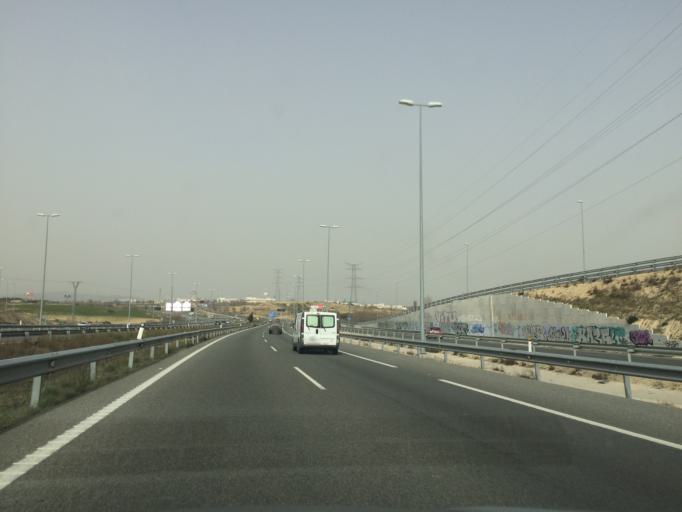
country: ES
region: Madrid
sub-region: Provincia de Madrid
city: Las Rozas de Madrid
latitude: 40.4882
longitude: -3.8954
